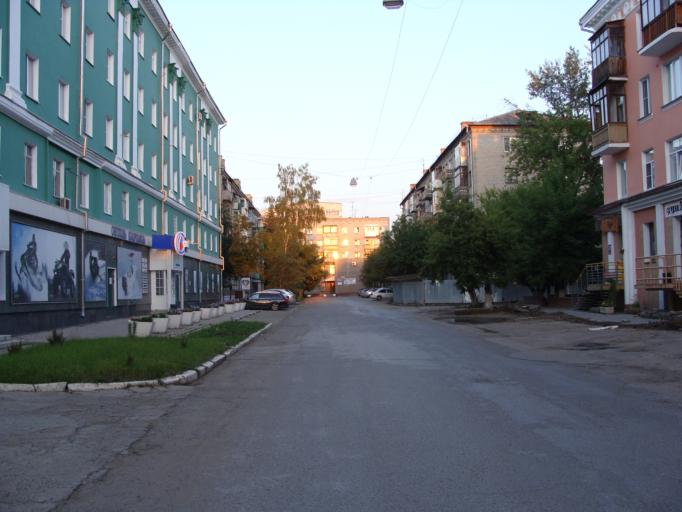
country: RU
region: Altai Krai
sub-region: Gorod Barnaulskiy
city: Barnaul
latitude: 53.3520
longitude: 83.7715
